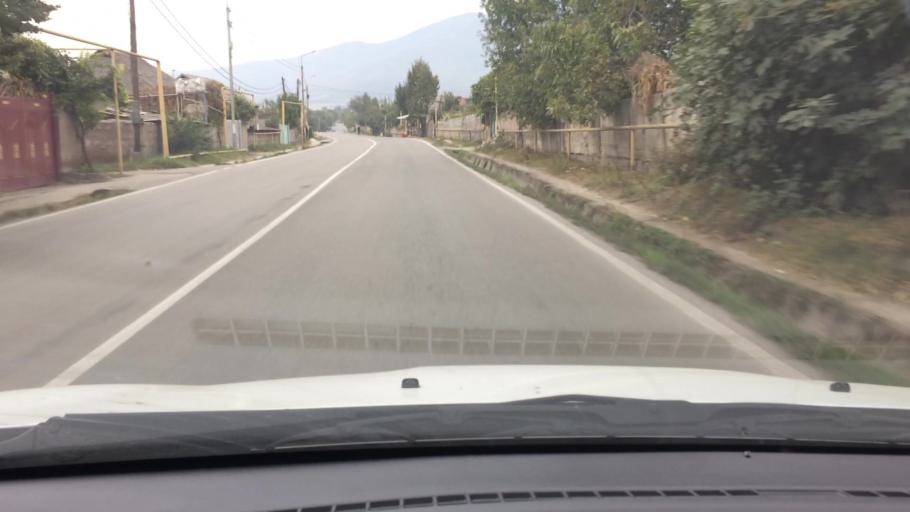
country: AM
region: Tavush
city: Bagratashen
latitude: 41.2422
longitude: 44.7990
